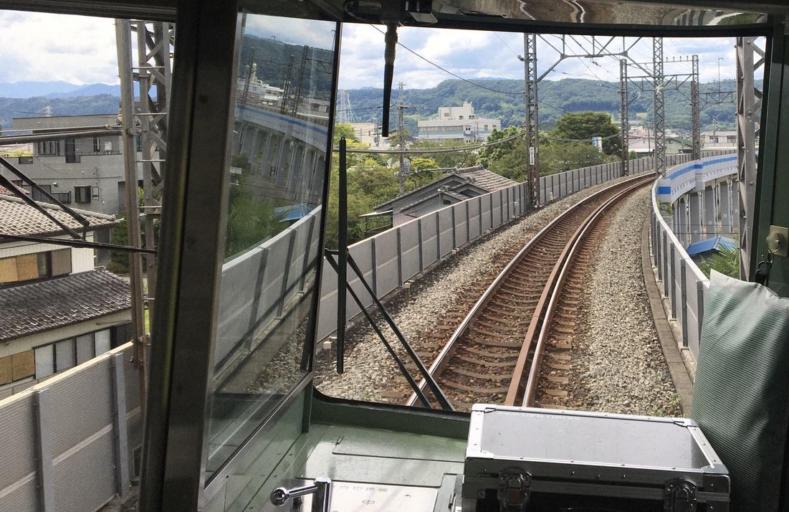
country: JP
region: Saitama
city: Chichibu
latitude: 35.9843
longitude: 139.0840
